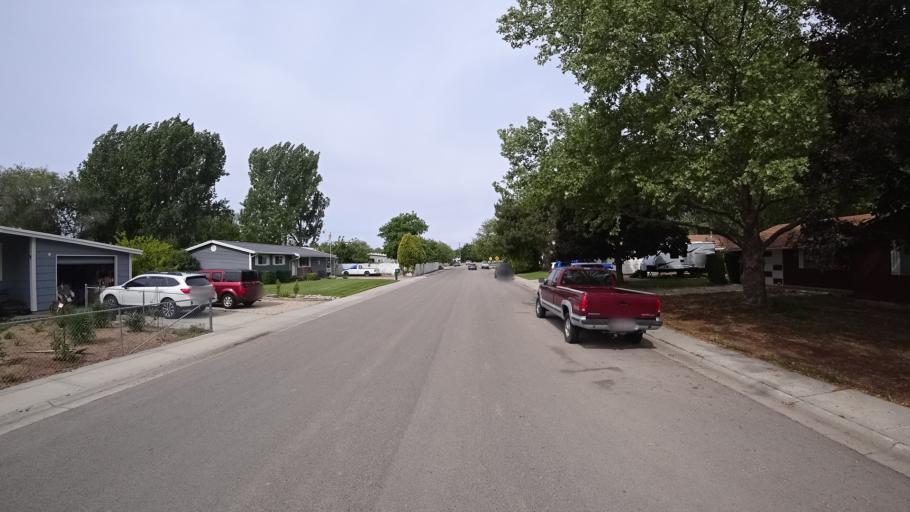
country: US
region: Idaho
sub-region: Ada County
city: Meridian
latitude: 43.5387
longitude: -116.3120
